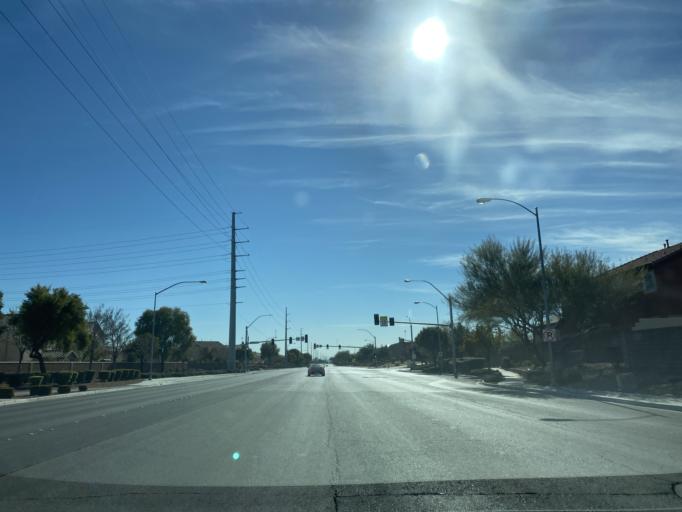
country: US
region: Nevada
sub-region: Clark County
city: North Las Vegas
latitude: 36.2702
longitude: -115.1441
